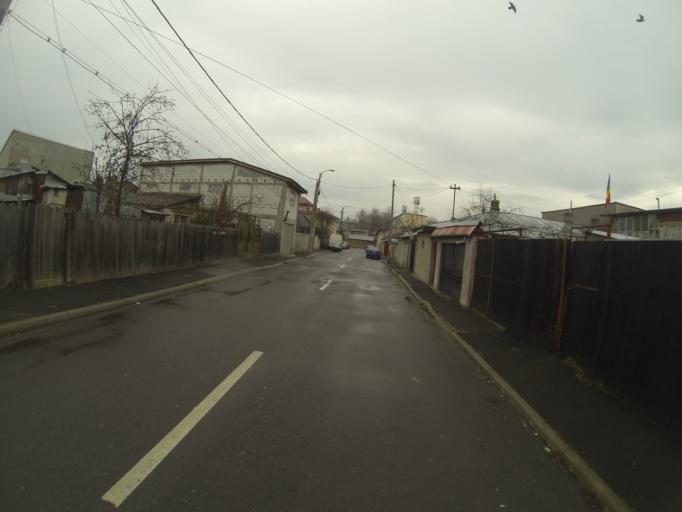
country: RO
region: Bucuresti
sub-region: Municipiul Bucuresti
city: Bucuresti
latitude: 44.4013
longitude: 26.0783
